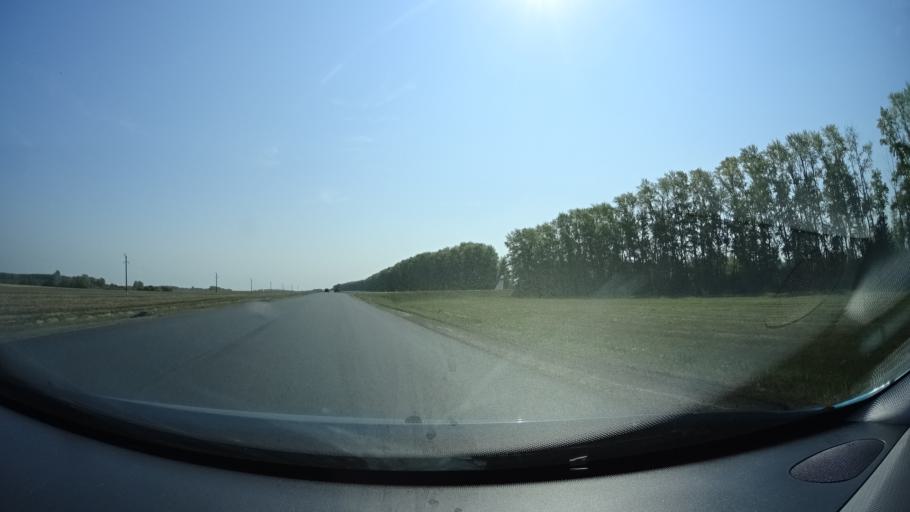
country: RU
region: Bashkortostan
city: Karmaskaly
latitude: 54.4095
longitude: 56.0702
